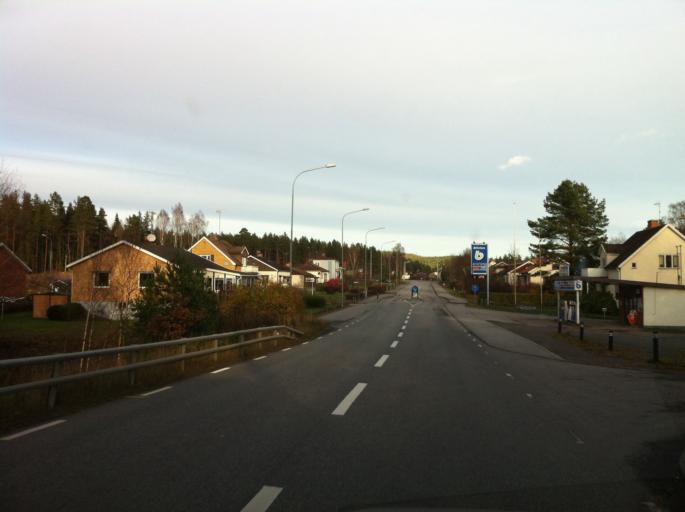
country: SE
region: Kalmar
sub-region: Hultsfreds Kommun
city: Virserum
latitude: 57.4119
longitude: 15.6185
